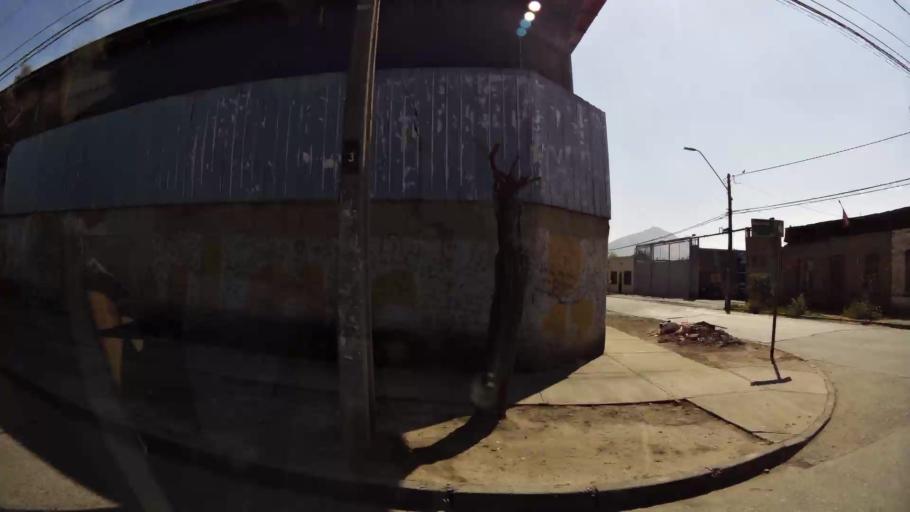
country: CL
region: Santiago Metropolitan
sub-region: Provincia de Santiago
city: Lo Prado
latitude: -33.4134
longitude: -70.6856
